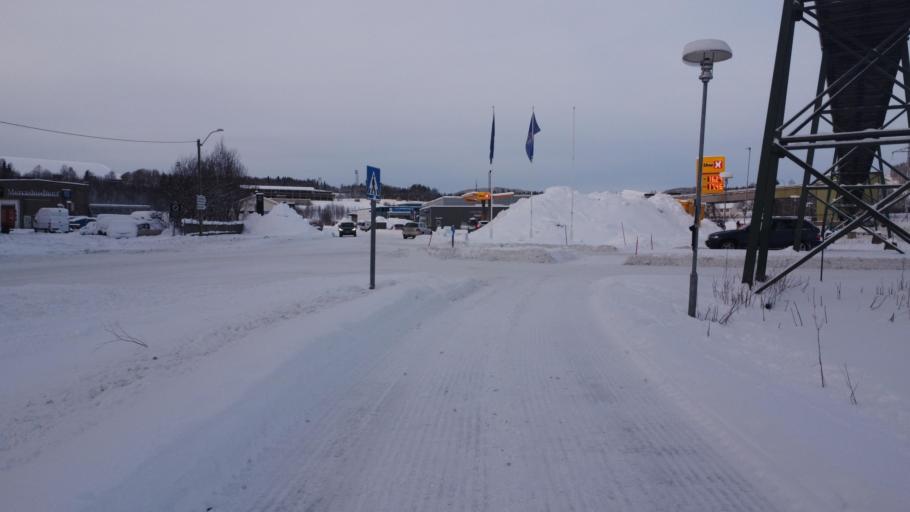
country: NO
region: Nordland
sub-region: Rana
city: Mo i Rana
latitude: 66.3209
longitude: 14.1698
